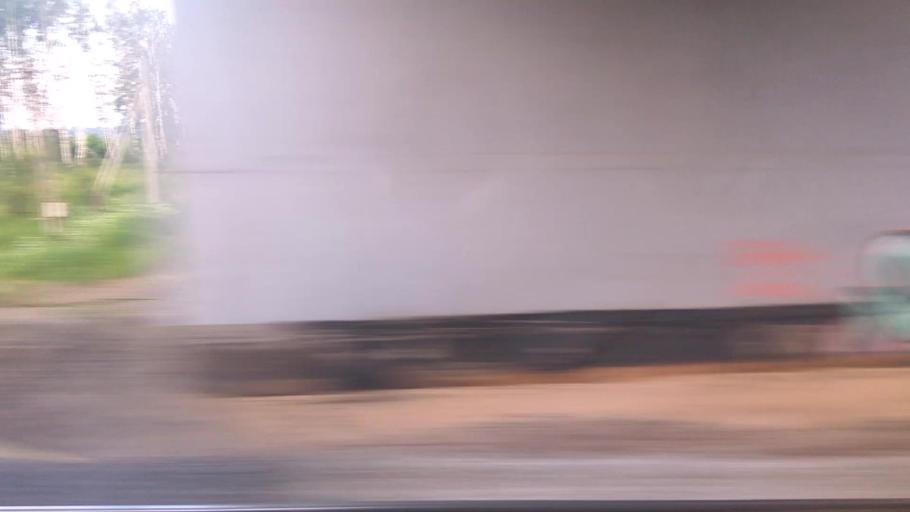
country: RU
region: Moskovskaya
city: Mikhnevo
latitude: 55.0840
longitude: 37.9731
